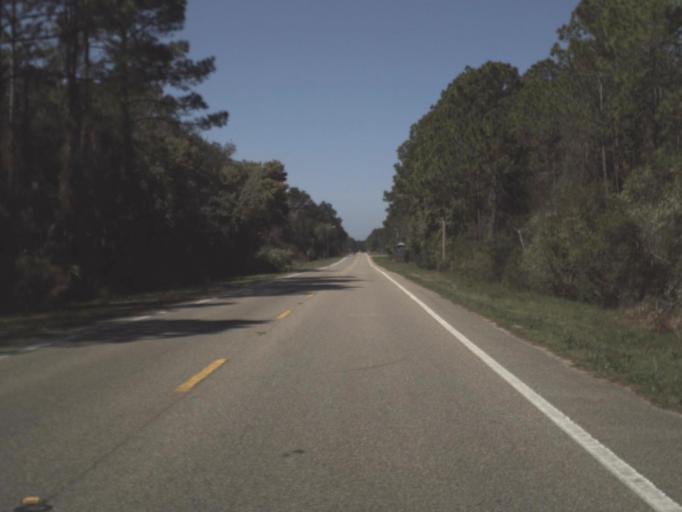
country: US
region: Florida
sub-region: Gulf County
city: Port Saint Joe
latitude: 29.7766
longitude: -85.2751
